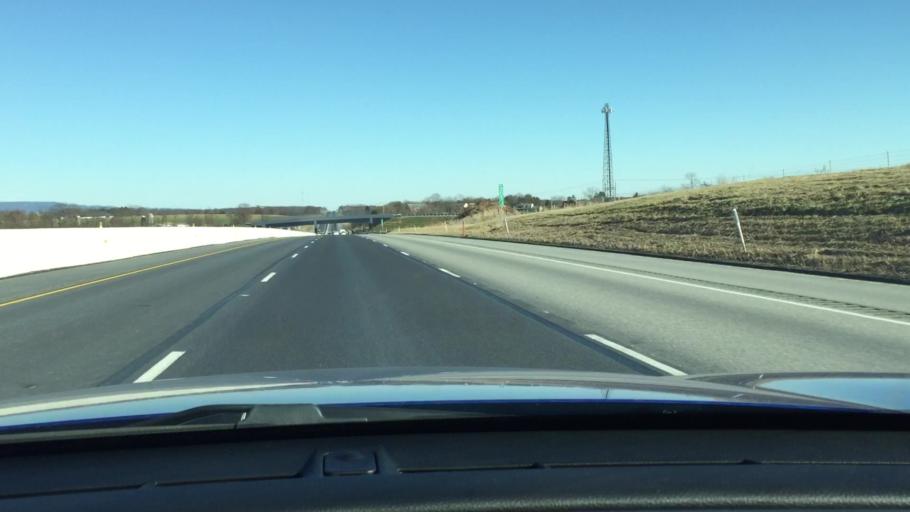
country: US
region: Pennsylvania
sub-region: Cumberland County
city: Shippensburg
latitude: 40.1731
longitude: -77.5486
